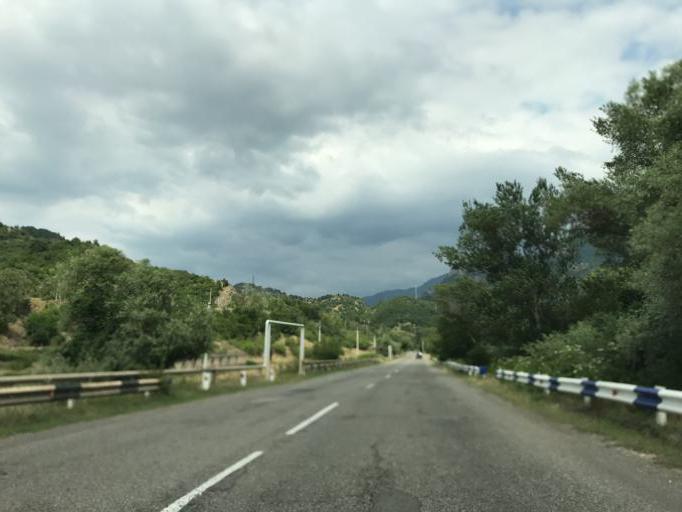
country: AM
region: Tavush
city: Haghartsin
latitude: 40.7687
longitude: 45.0067
